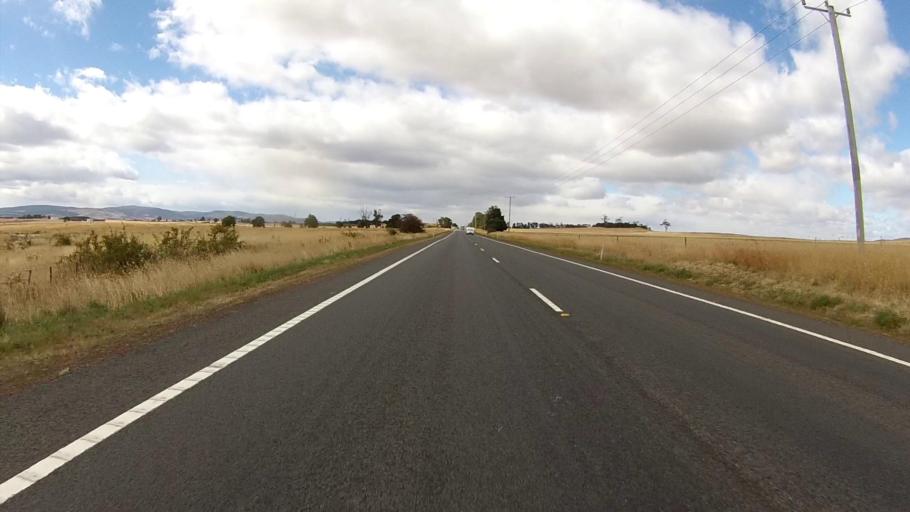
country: AU
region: Tasmania
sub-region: Northern Midlands
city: Evandale
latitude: -41.8977
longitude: 147.4744
